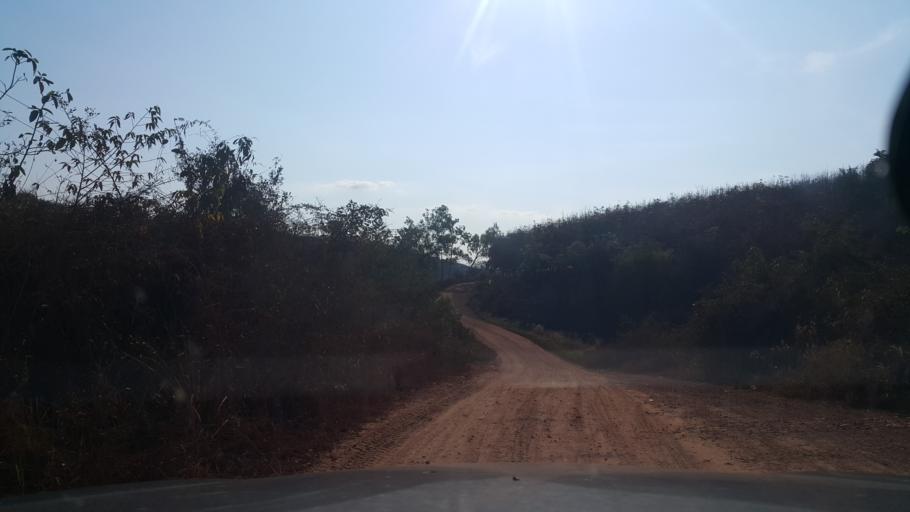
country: TH
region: Loei
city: Chiang Khan
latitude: 17.8098
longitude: 101.6187
